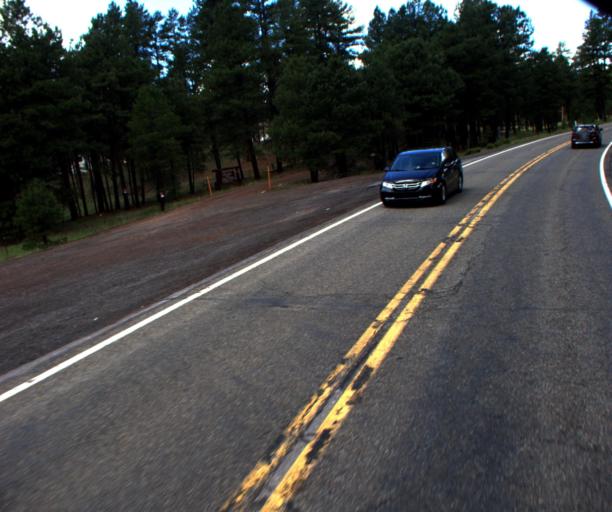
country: US
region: Arizona
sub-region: Coconino County
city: Flagstaff
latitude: 35.2681
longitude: -111.7400
